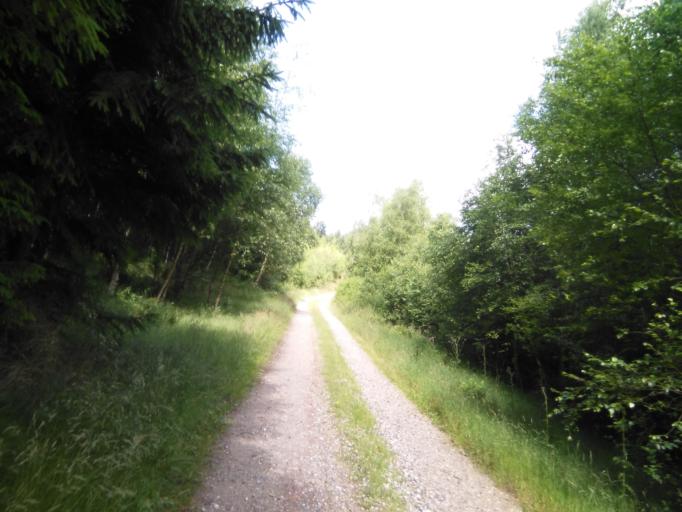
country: DK
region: Central Jutland
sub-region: Silkeborg Kommune
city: Virklund
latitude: 56.0666
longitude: 9.4487
